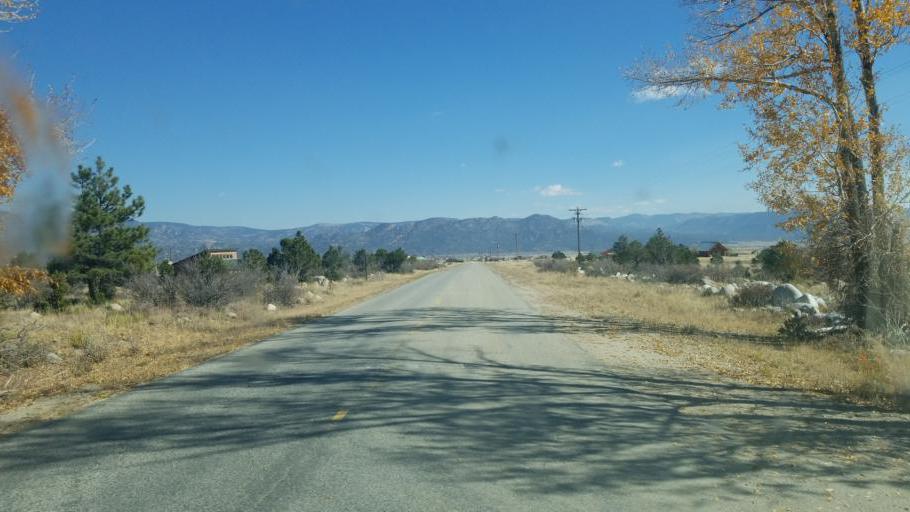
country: US
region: Colorado
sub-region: Chaffee County
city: Buena Vista
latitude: 38.8146
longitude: -106.2031
